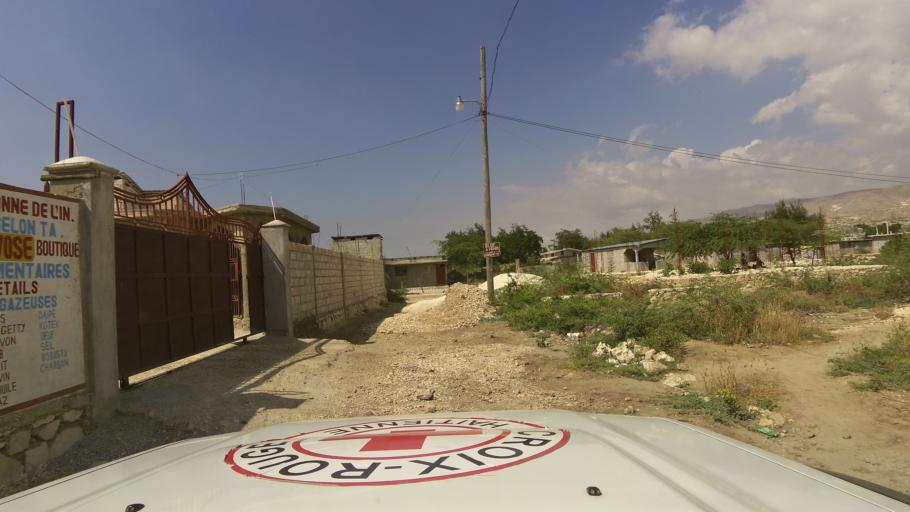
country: HT
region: Ouest
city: Croix des Bouquets
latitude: 18.6427
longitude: -72.2643
